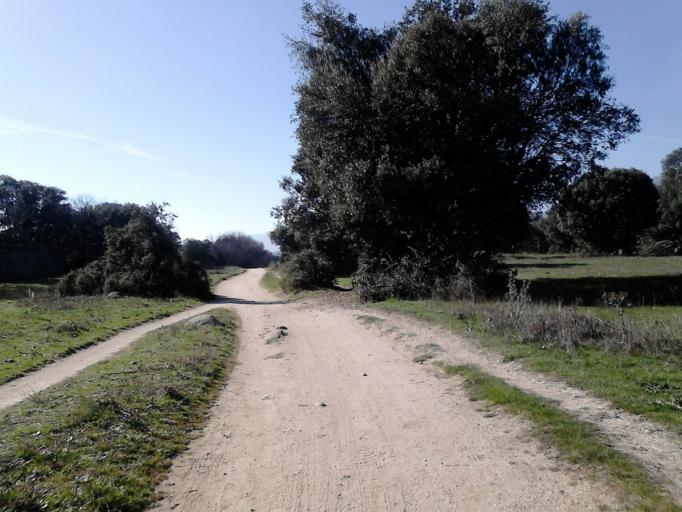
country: ES
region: Madrid
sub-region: Provincia de Madrid
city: Navalquejigo
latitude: 40.6123
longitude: -4.0779
